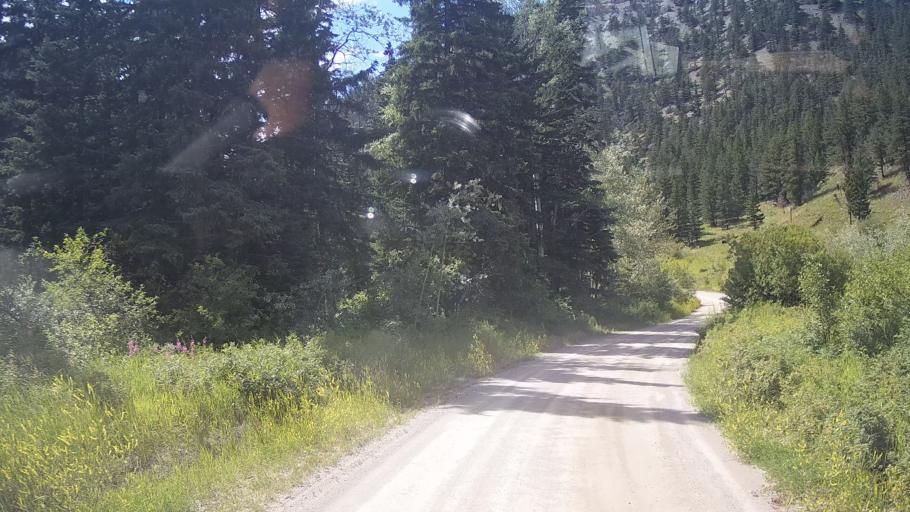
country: CA
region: British Columbia
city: Lillooet
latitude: 51.2588
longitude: -121.9930
